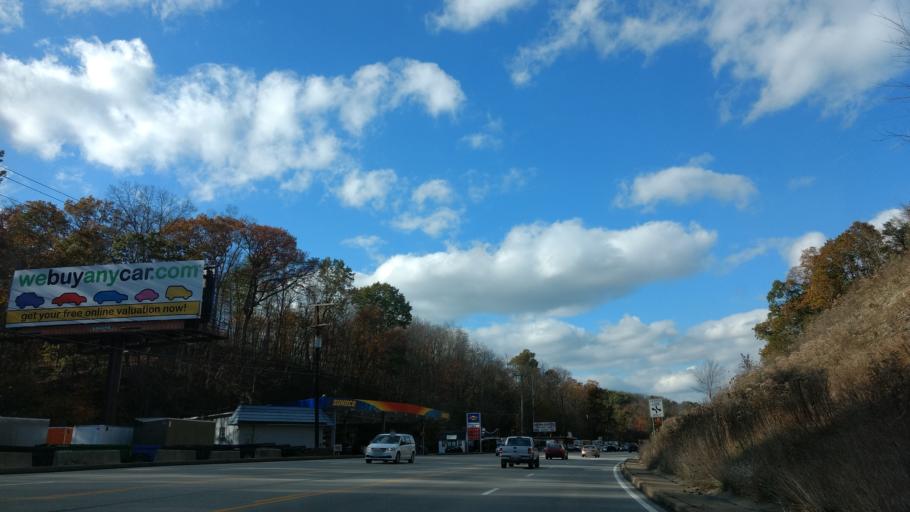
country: US
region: Pennsylvania
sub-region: Allegheny County
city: Jefferson Hills
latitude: 40.3056
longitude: -79.9344
